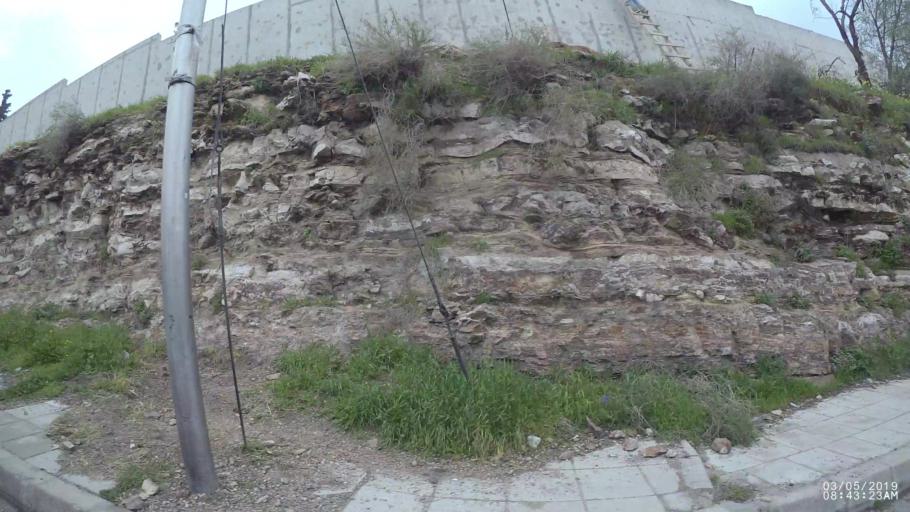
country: JO
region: Amman
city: Amman
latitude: 31.9563
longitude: 35.9444
